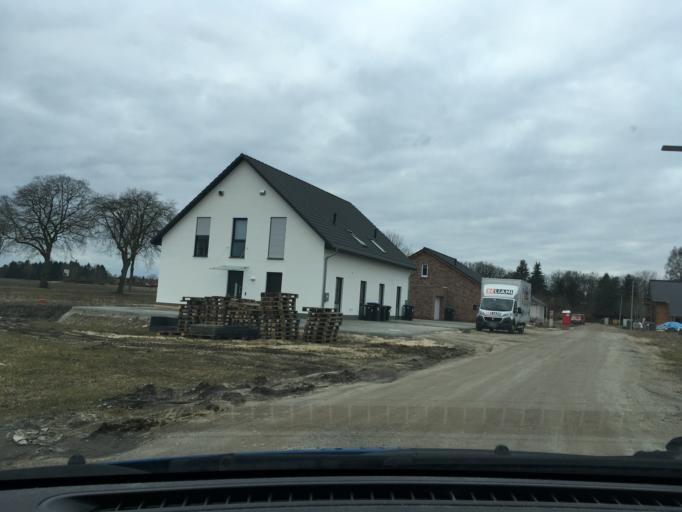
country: DE
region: Lower Saxony
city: Wietzendorf
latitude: 52.9120
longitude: 9.9827
